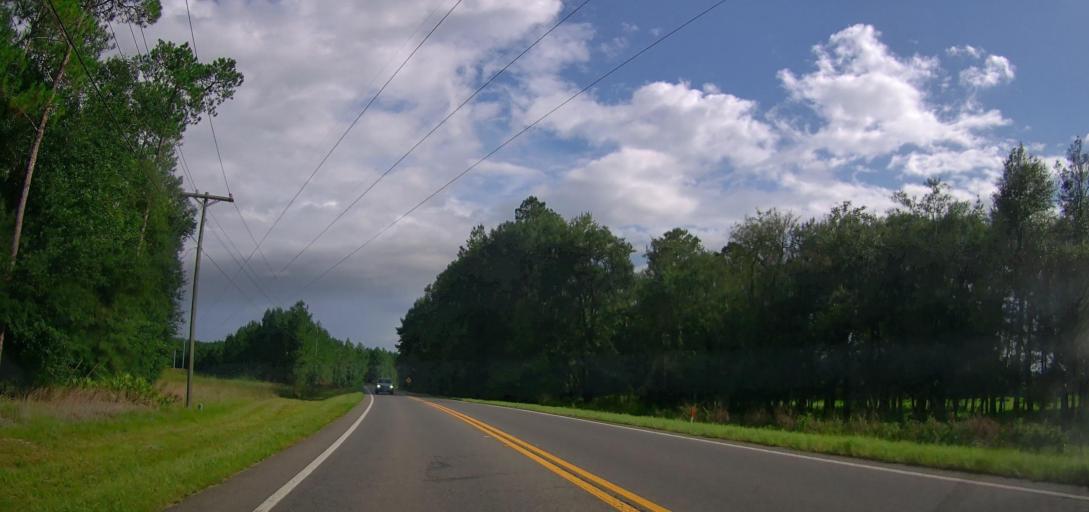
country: US
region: Georgia
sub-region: Coffee County
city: Douglas
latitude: 31.4564
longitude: -82.8887
